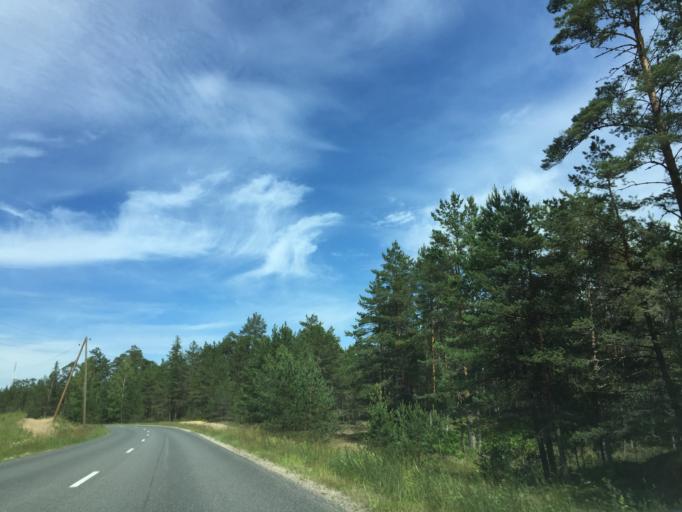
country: LV
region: Dundaga
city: Dundaga
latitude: 57.6428
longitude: 22.5705
